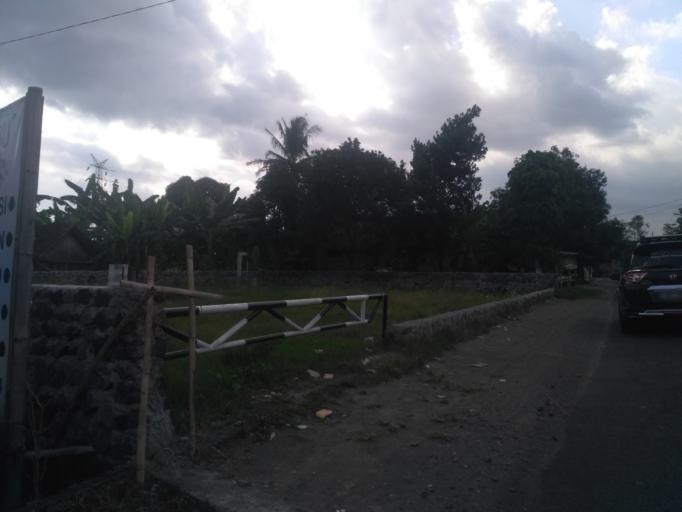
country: ID
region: Daerah Istimewa Yogyakarta
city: Godean
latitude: -7.7576
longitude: 110.3204
